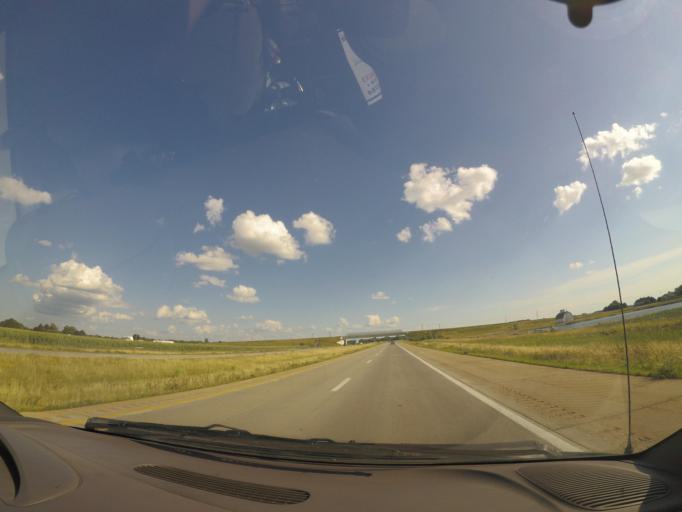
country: US
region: Ohio
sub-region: Lucas County
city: Whitehouse
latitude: 41.4764
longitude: -83.7766
